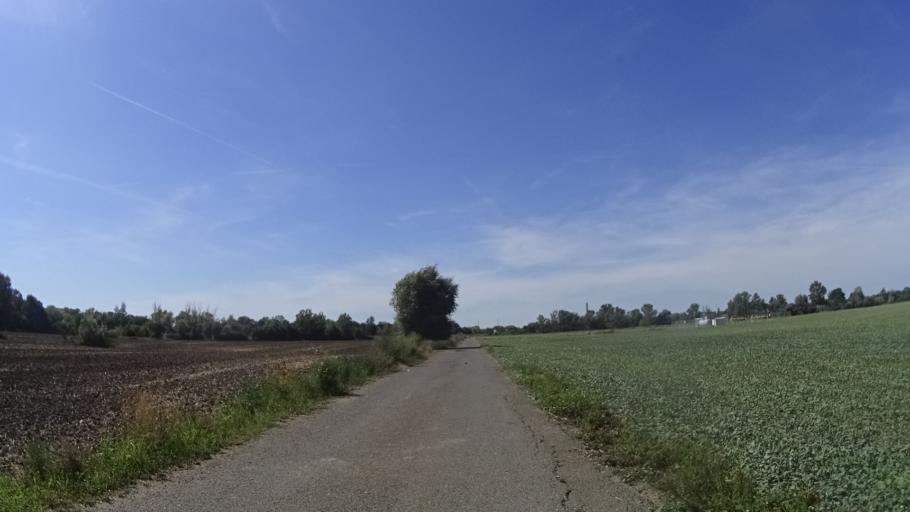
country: AT
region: Lower Austria
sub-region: Politischer Bezirk Ganserndorf
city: Angern an der March
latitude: 48.3731
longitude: 16.8507
